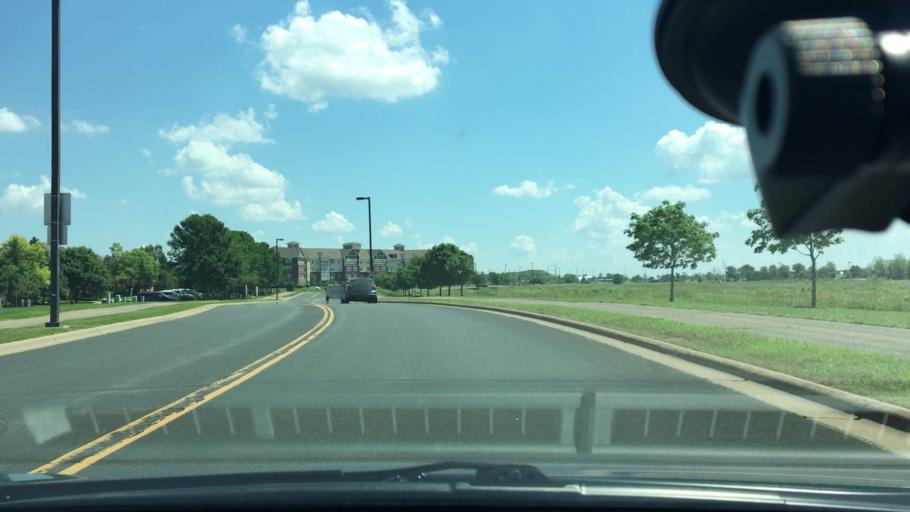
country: US
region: Minnesota
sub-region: Hennepin County
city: Maple Grove
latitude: 45.0982
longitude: -93.4385
